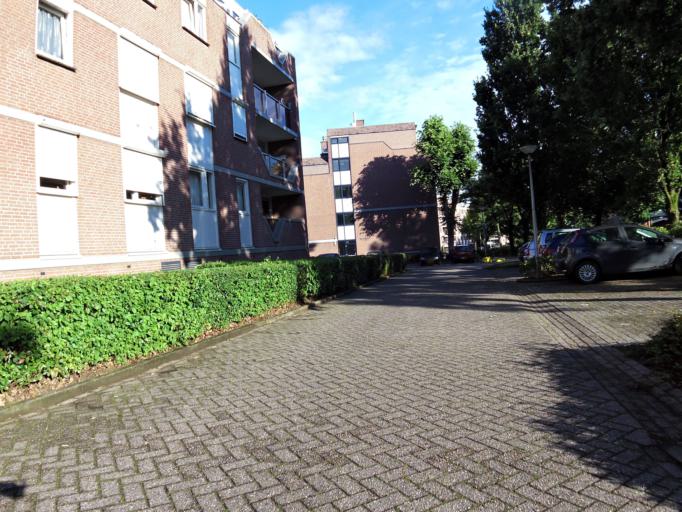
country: NL
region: Limburg
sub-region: Gemeente Heerlen
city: Heerlen
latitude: 50.8707
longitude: 5.9795
